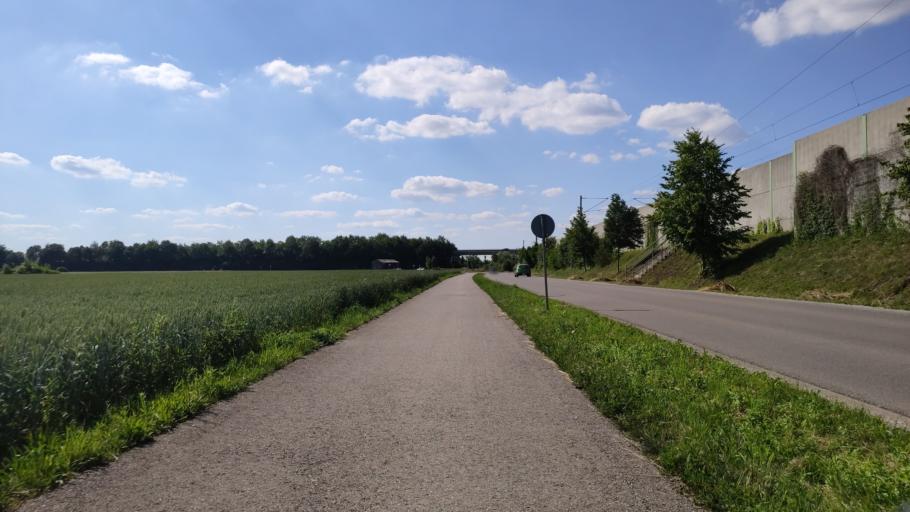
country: DE
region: Bavaria
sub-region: Swabia
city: Mering
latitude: 48.2685
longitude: 10.9782
